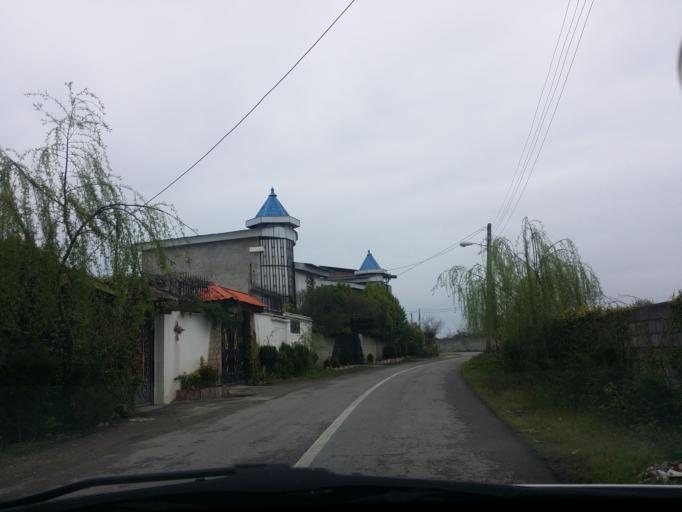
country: IR
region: Mazandaran
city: Chalus
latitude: 36.6754
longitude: 51.3790
